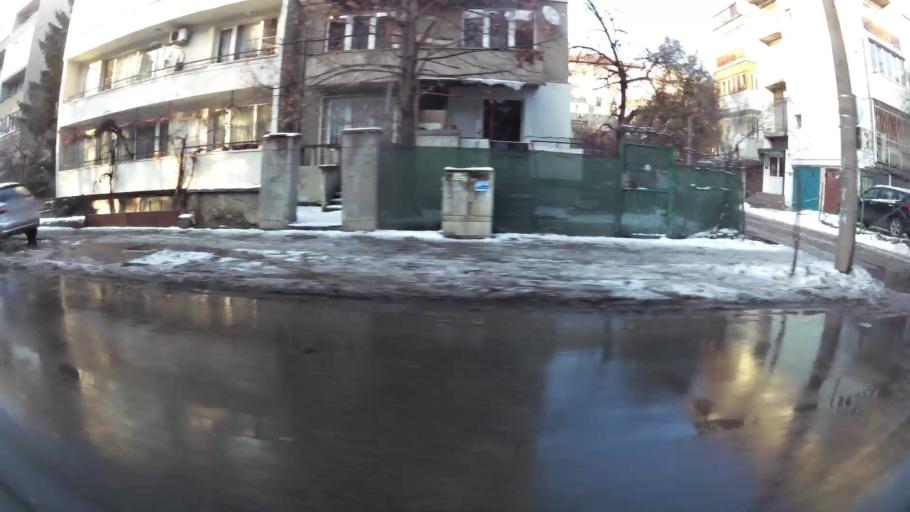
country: BG
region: Sofia-Capital
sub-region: Stolichna Obshtina
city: Sofia
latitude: 42.6827
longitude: 23.3652
